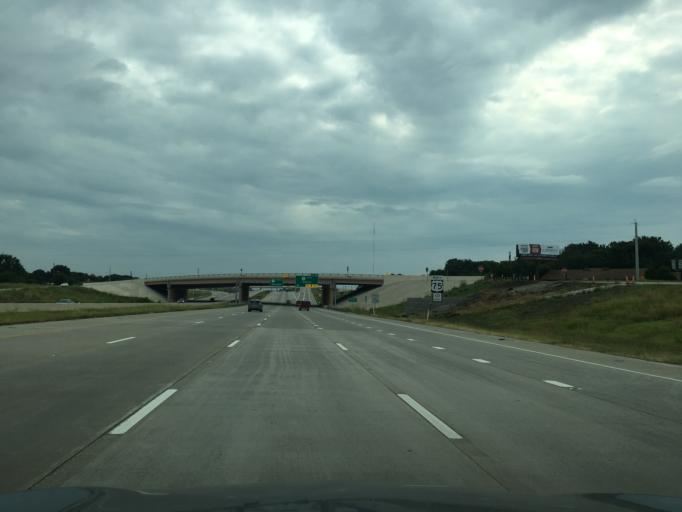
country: US
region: Texas
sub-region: Collin County
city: Melissa
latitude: 33.2586
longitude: -96.6072
